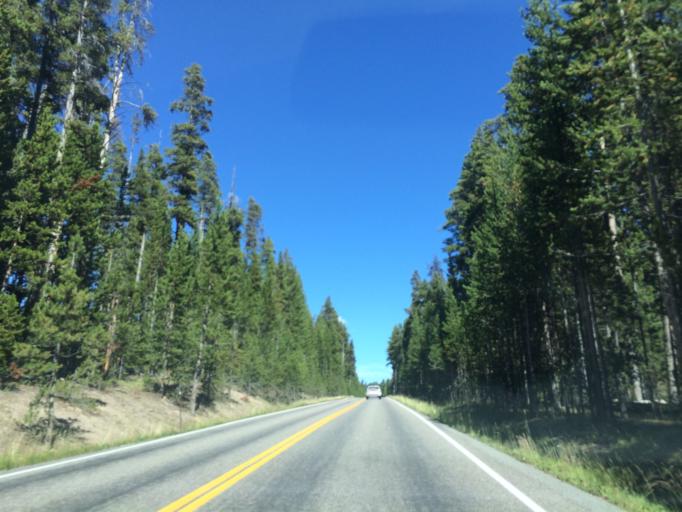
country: US
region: Montana
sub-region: Gallatin County
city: West Yellowstone
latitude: 44.5727
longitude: -110.3844
